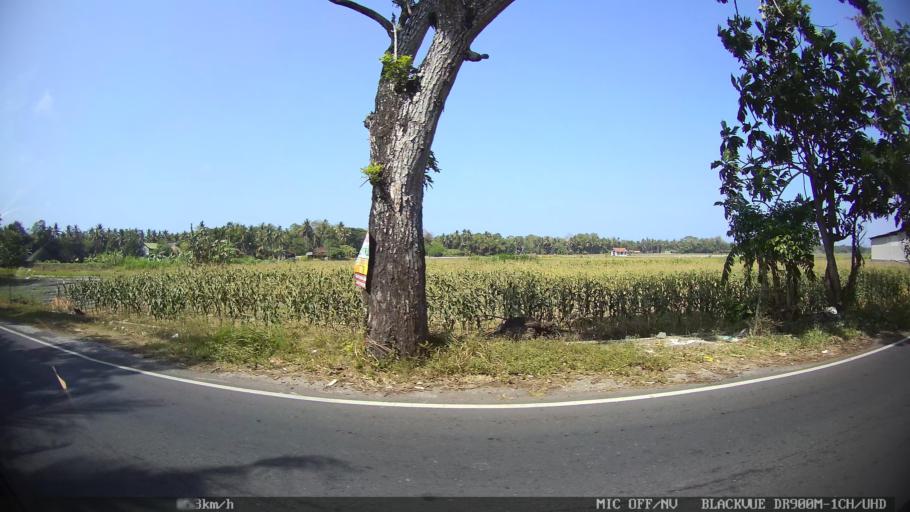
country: ID
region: Daerah Istimewa Yogyakarta
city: Srandakan
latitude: -7.9361
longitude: 110.2217
